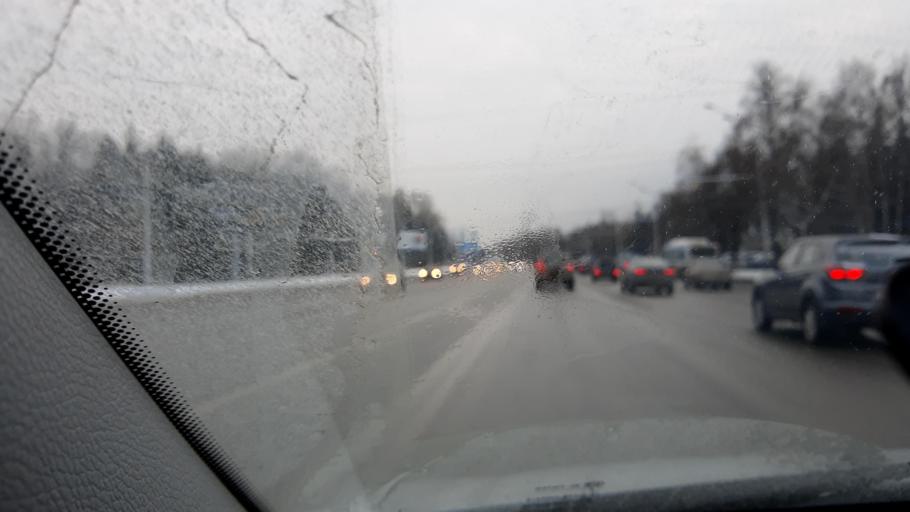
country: RU
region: Bashkortostan
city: Ufa
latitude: 54.7975
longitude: 56.0414
